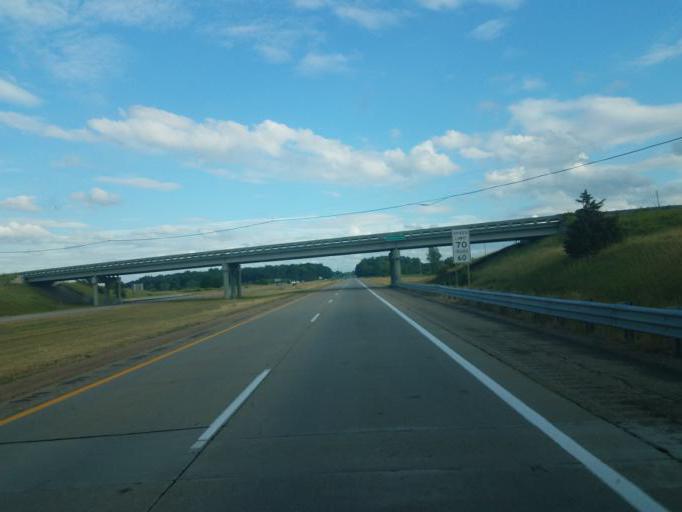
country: US
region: Indiana
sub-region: Steuben County
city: Fremont
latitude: 41.7863
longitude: -84.9923
